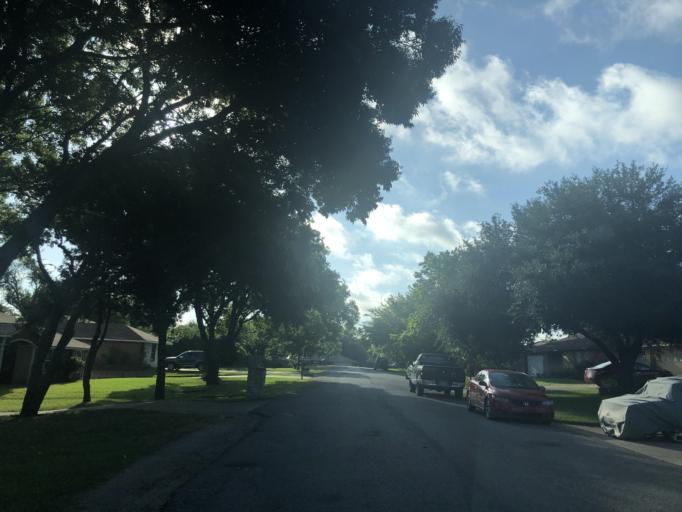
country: US
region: Texas
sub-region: Dallas County
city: Duncanville
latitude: 32.6671
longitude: -96.9122
